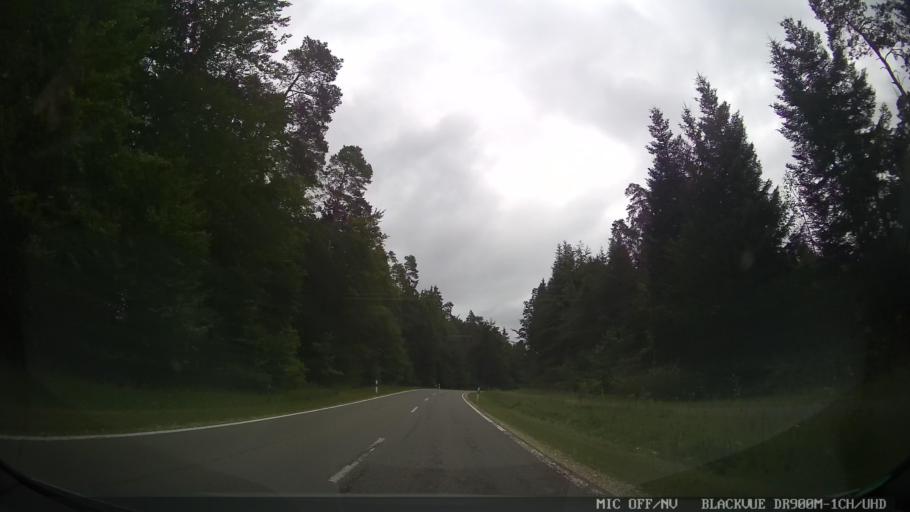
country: DE
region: Baden-Wuerttemberg
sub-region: Freiburg Region
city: Neuhausen ob Eck
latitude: 47.9592
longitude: 8.9331
